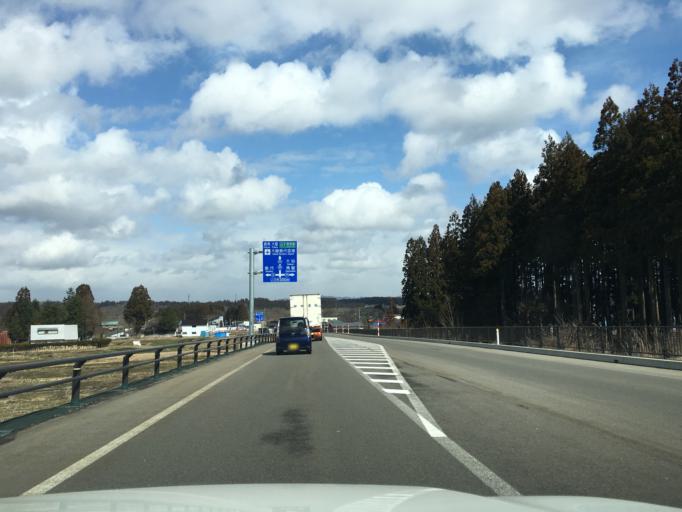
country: JP
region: Akita
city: Takanosu
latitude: 40.1167
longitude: 140.3770
